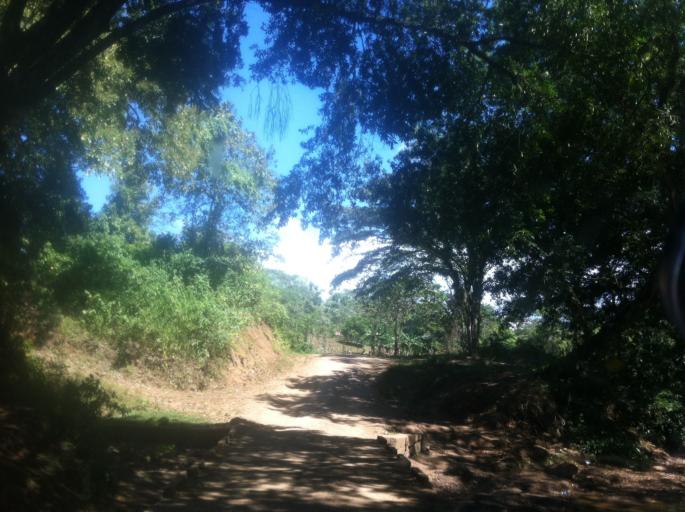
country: CR
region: Alajuela
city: Los Chiles
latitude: 11.2508
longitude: -84.4430
